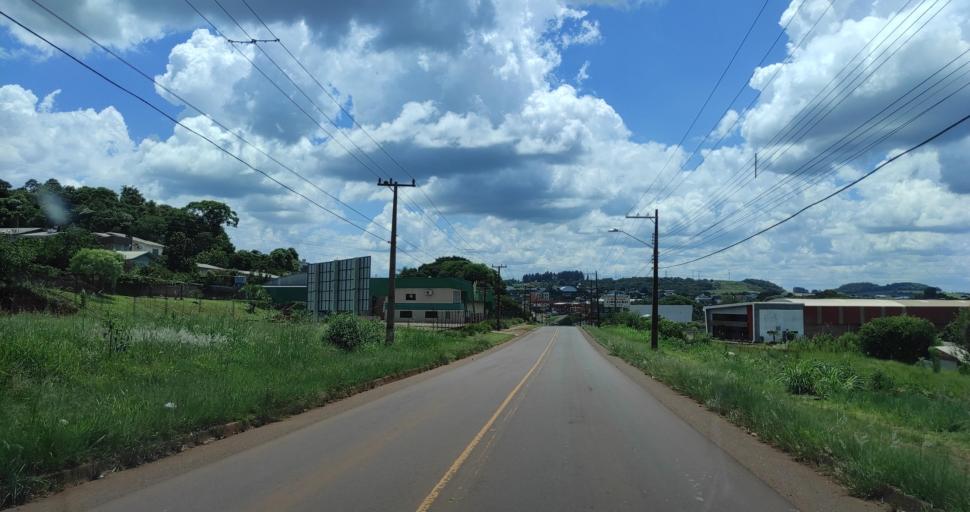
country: BR
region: Santa Catarina
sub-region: Xanxere
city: Xanxere
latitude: -26.8646
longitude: -52.4085
